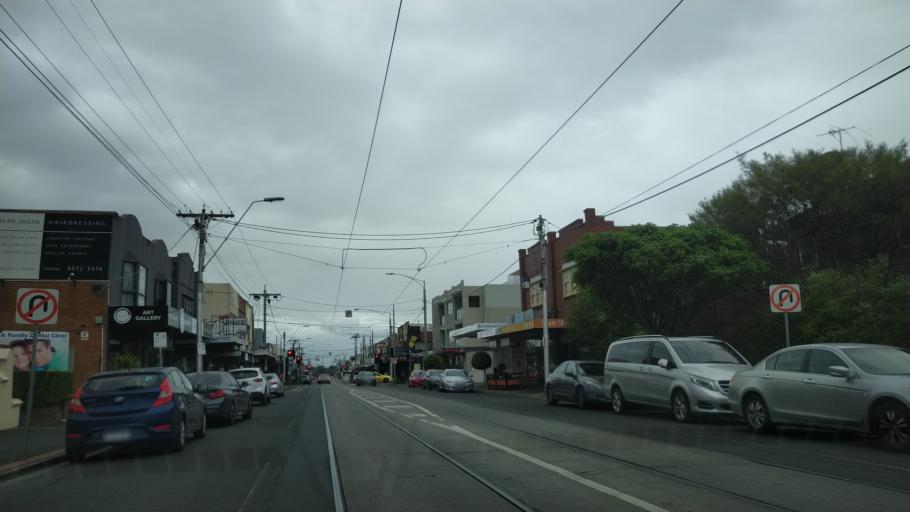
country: AU
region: Victoria
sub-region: Glen Eira
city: Glen Huntly
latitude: -37.8891
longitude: 145.0396
